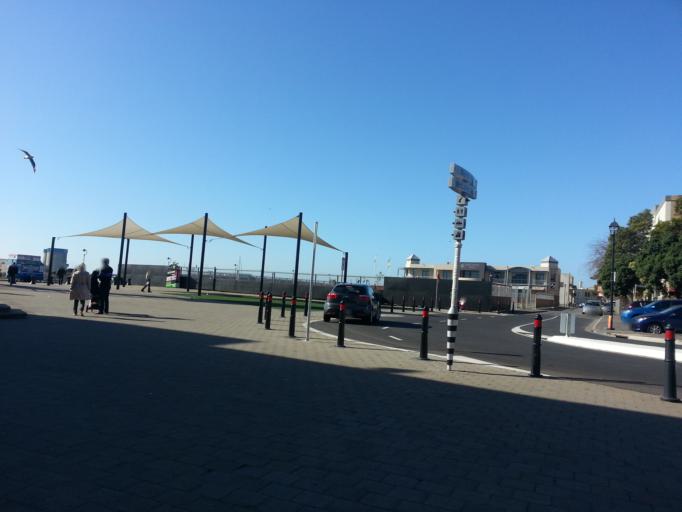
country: AU
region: South Australia
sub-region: Port Adelaide Enfield
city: Birkenhead
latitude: -34.8429
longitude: 138.5043
